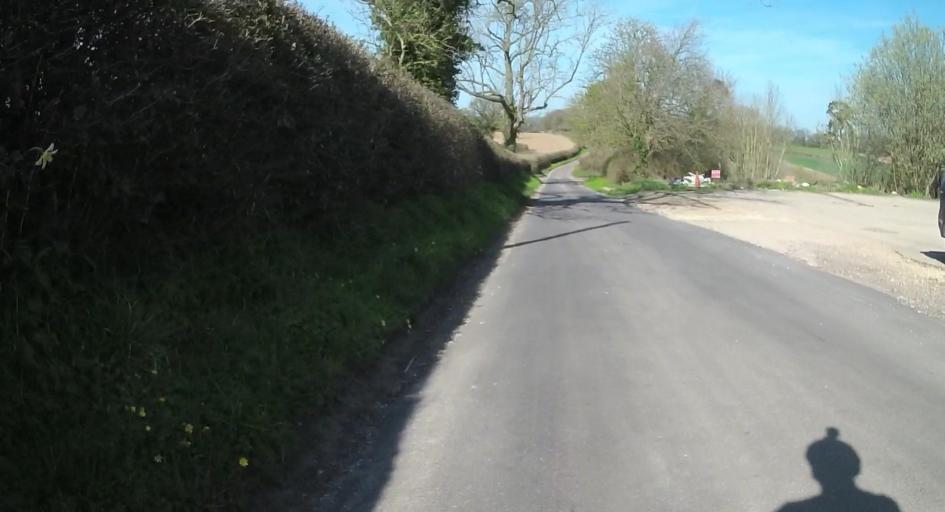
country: GB
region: England
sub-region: Hampshire
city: Highclere
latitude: 51.2712
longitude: -1.4140
